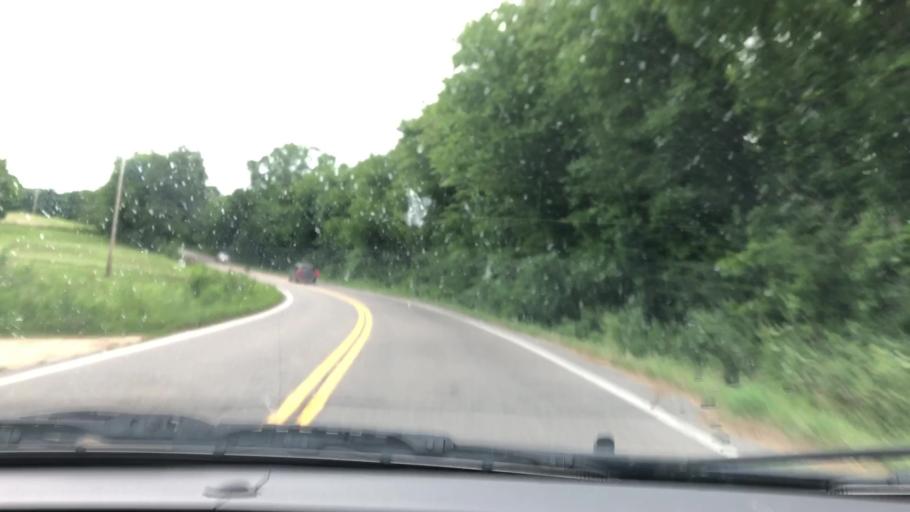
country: US
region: Tennessee
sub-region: Maury County
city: Columbia
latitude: 35.6840
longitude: -87.0109
